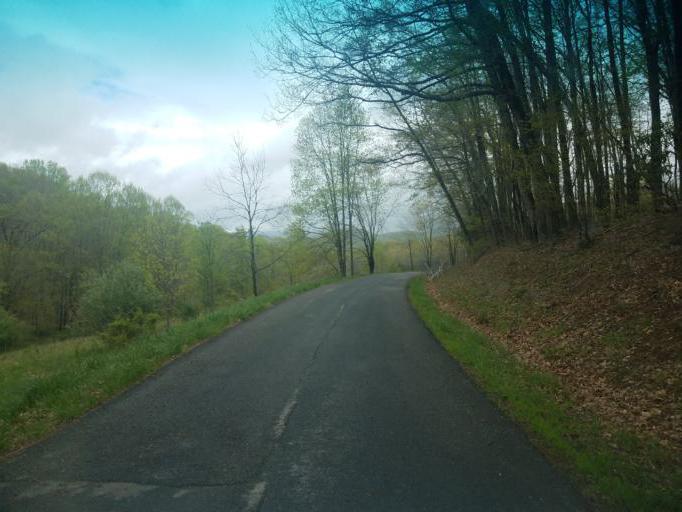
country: US
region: Virginia
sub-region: Smyth County
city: Atkins
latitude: 36.9671
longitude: -81.3905
